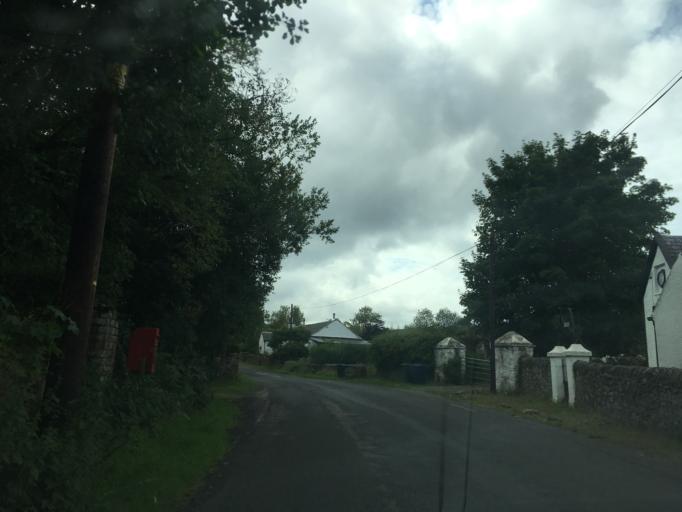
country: GB
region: Scotland
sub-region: Argyll and Bute
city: Tarbert
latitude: 55.8863
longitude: -5.2657
